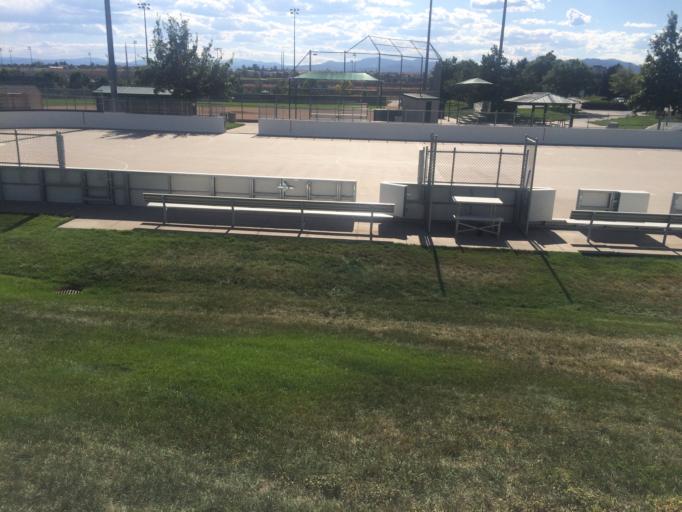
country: US
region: Colorado
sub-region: Broomfield County
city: Broomfield
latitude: 39.9066
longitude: -105.0743
